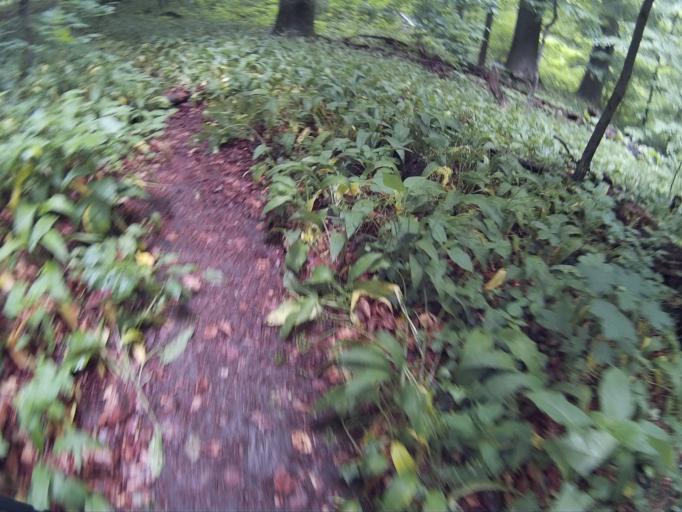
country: HU
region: Veszprem
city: Sumeg
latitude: 46.9033
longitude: 17.2587
